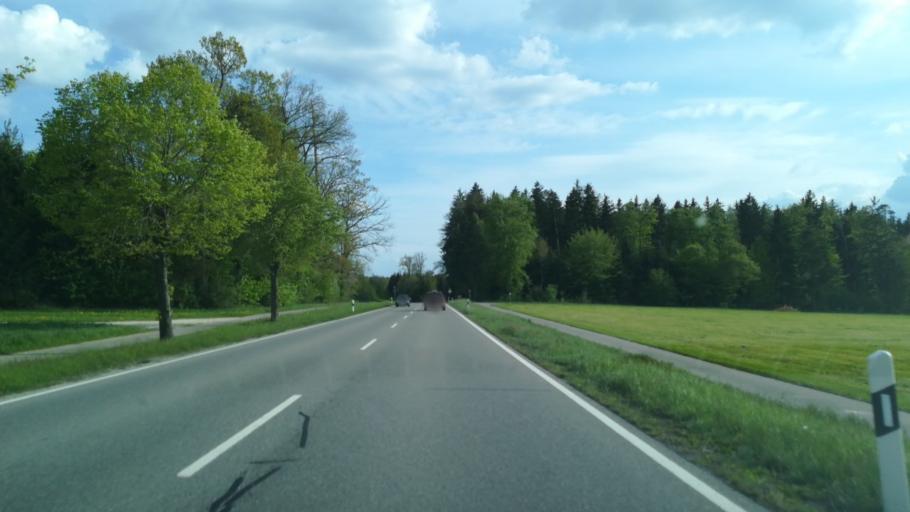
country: DE
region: Baden-Wuerttemberg
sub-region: Freiburg Region
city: Muhlingen
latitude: 47.9469
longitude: 9.0445
